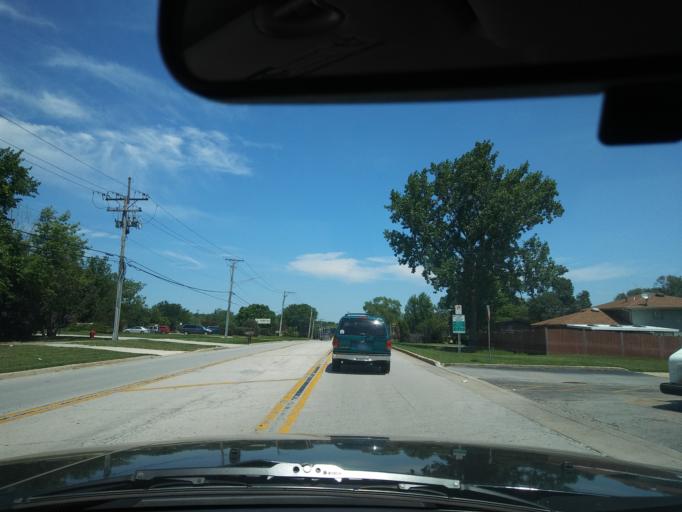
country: US
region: Illinois
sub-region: Cook County
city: Oak Forest
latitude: 41.6053
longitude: -87.7560
